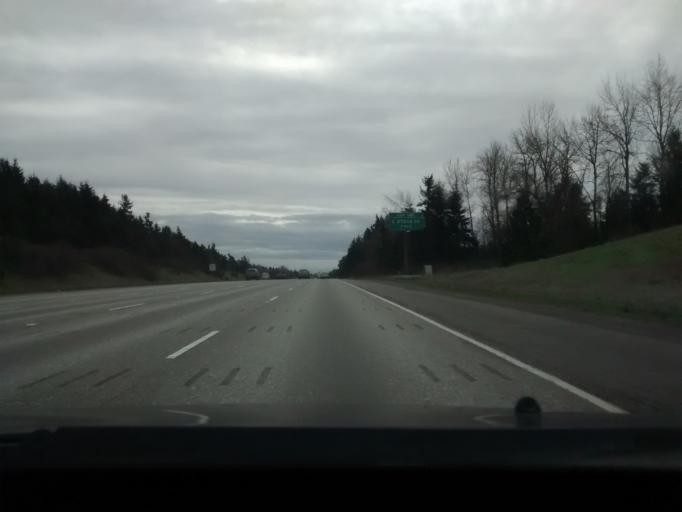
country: US
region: Washington
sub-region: King County
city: Des Moines
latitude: 47.3765
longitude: -122.2921
